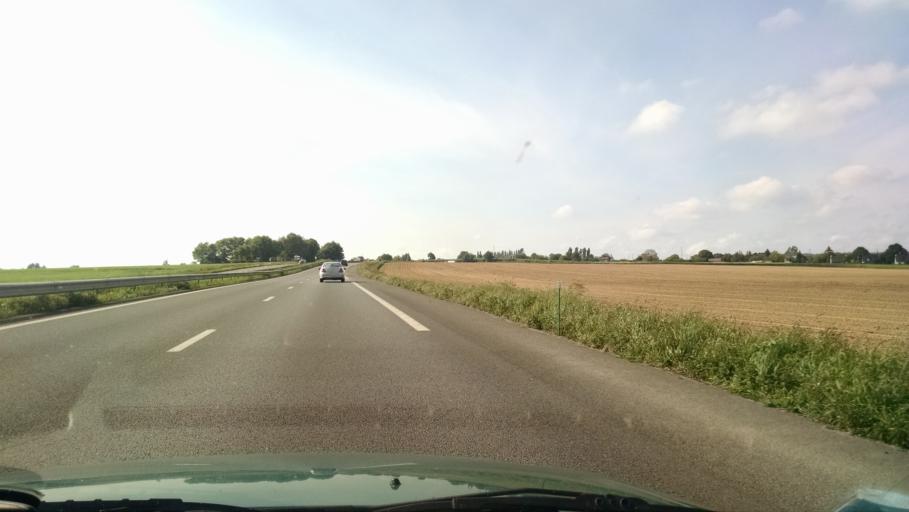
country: FR
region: Brittany
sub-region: Departement des Cotes-d'Armor
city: Plestan
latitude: 48.4388
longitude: -2.4745
